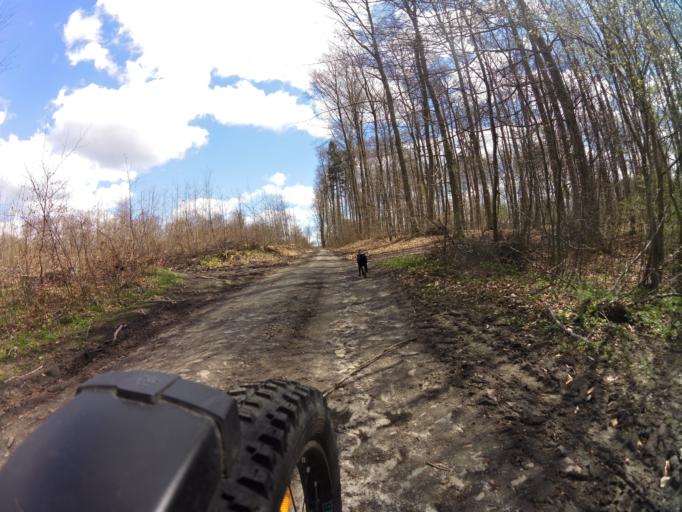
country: PL
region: West Pomeranian Voivodeship
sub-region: Powiat gryficki
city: Gryfice
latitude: 53.8439
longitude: 15.1782
